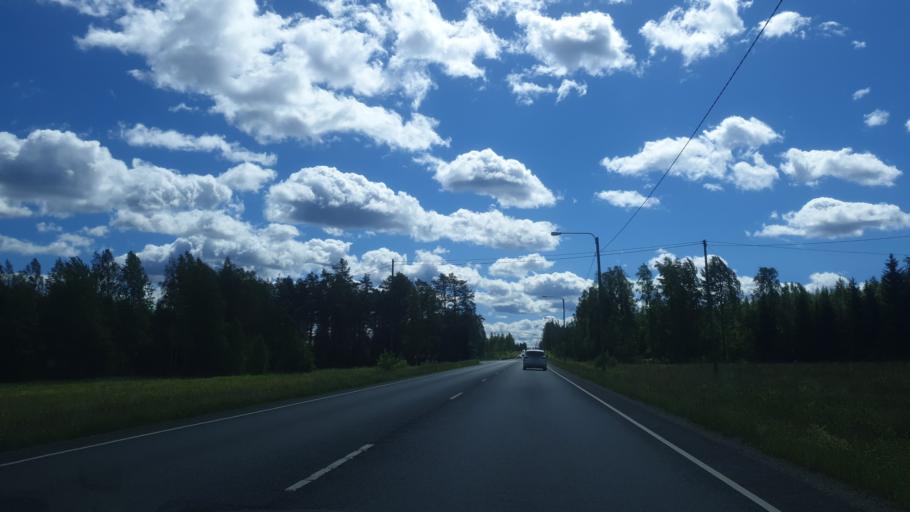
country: FI
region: Northern Savo
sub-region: Varkaus
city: Leppaevirta
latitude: 62.6342
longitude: 27.6134
